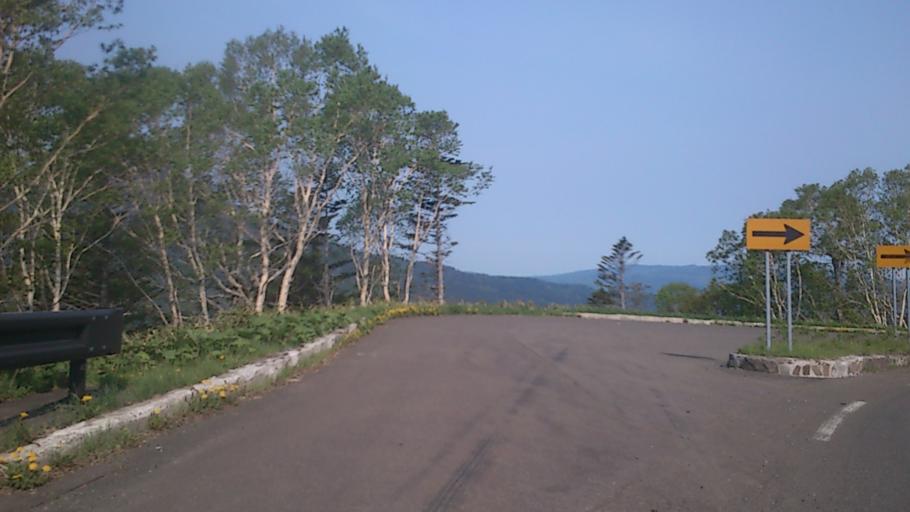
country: JP
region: Hokkaido
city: Bihoro
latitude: 43.4554
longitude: 144.2214
